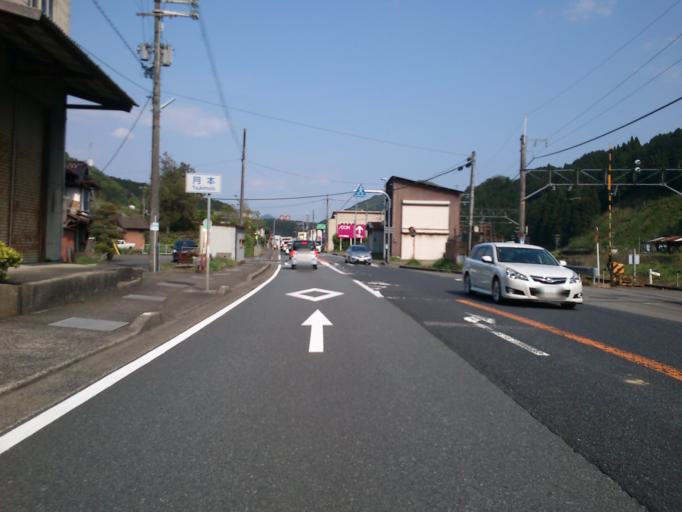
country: JP
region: Kyoto
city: Fukuchiyama
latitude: 35.3206
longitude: 134.9950
